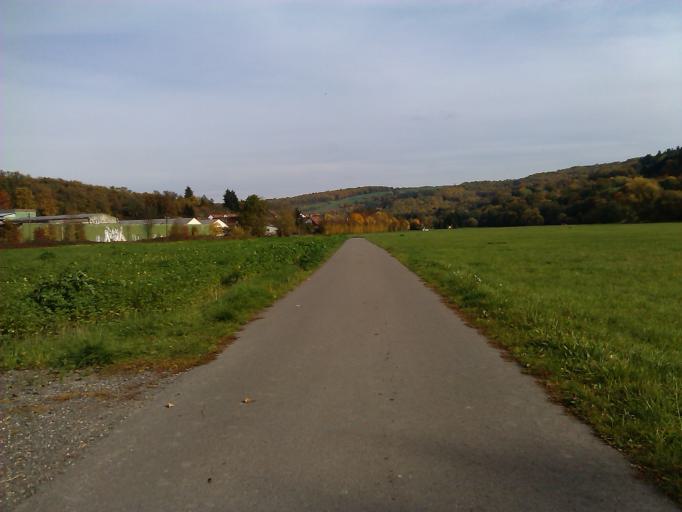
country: DE
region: Rheinland-Pfalz
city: Medard
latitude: 49.6644
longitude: 7.6041
